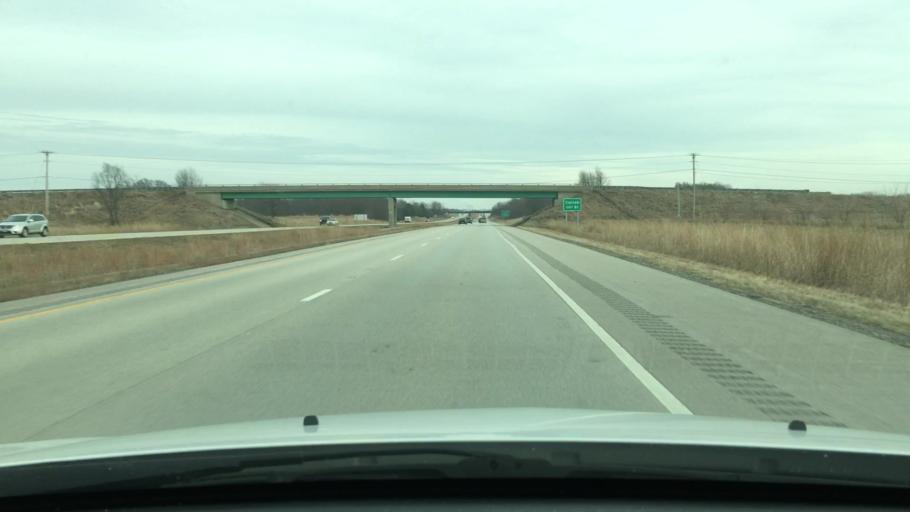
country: US
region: Illinois
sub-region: Sangamon County
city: Jerome
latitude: 39.7517
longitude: -89.7736
